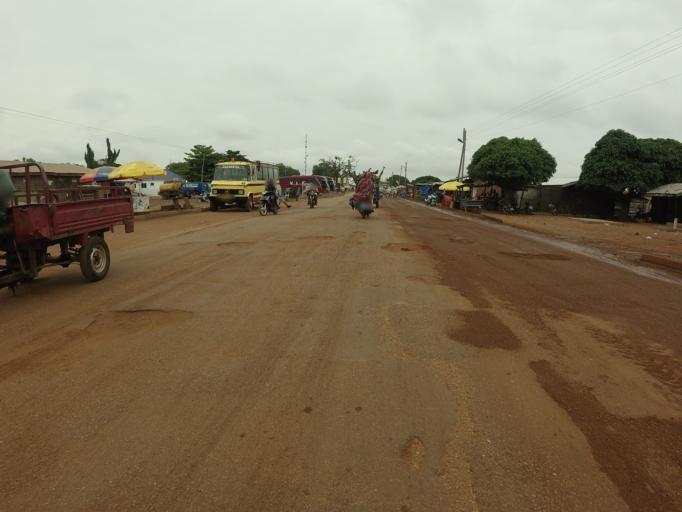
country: GH
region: Northern
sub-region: Yendi
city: Yendi
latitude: 9.4478
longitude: -0.0075
